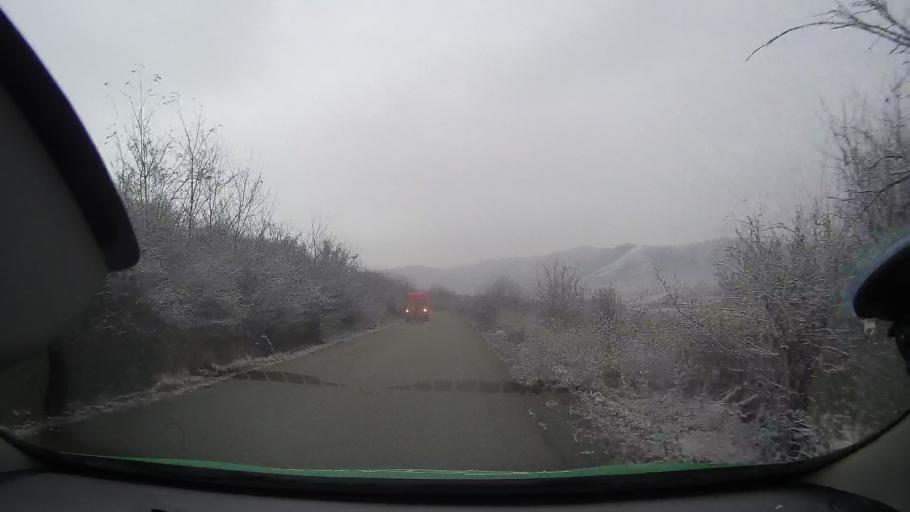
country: RO
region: Alba
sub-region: Comuna Hoparta
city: Hoparta
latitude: 46.3399
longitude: 23.9226
